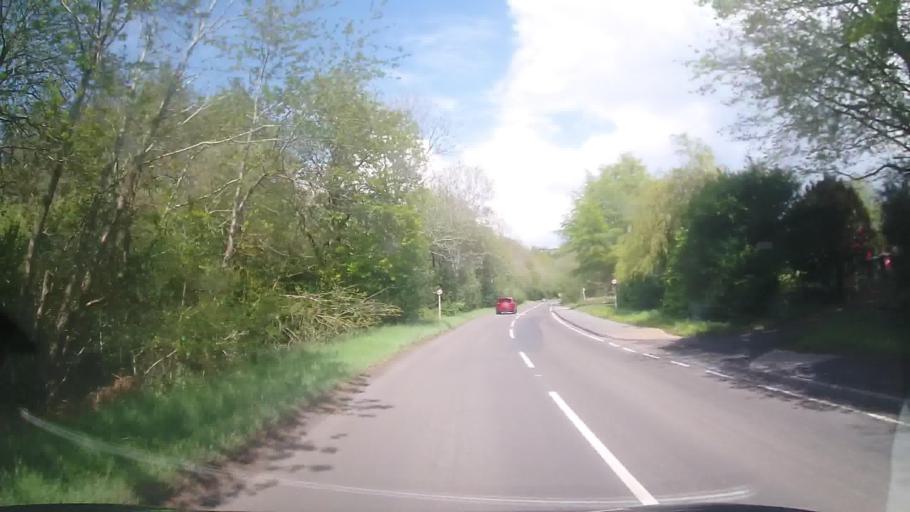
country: GB
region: Wales
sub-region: Gwynedd
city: Porthmadog
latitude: 52.9198
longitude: -4.1423
